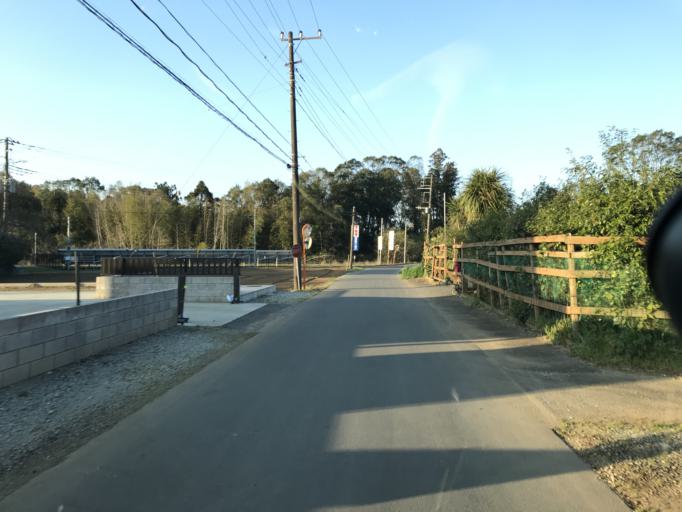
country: JP
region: Chiba
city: Yokaichiba
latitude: 35.7859
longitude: 140.5434
